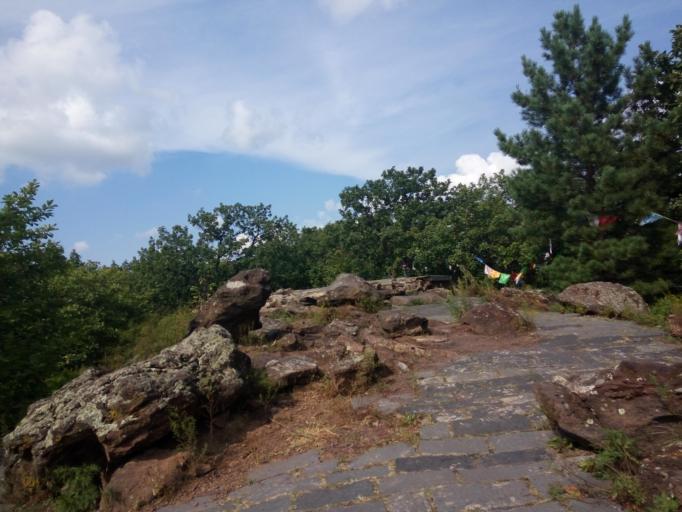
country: CN
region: Heilongjiang Sheng
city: Erjing
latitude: 48.6507
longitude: 126.1292
